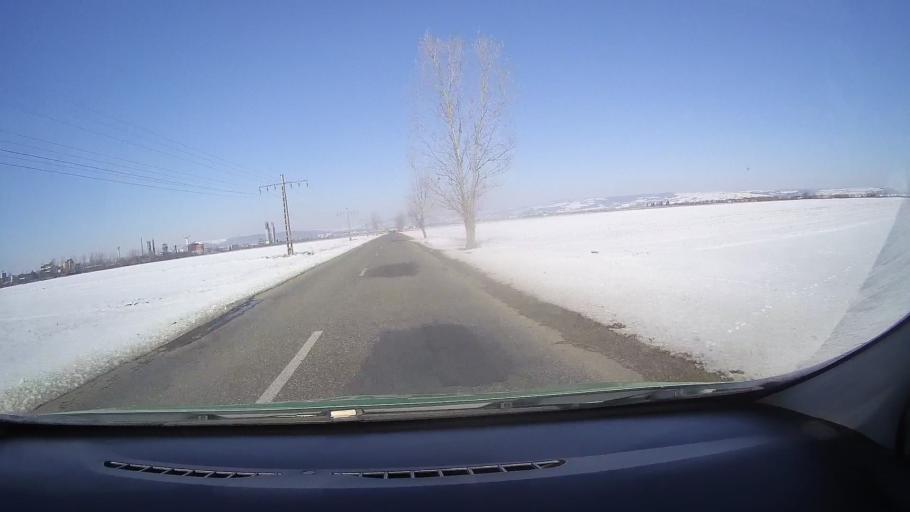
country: RO
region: Brasov
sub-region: Comuna Harseni
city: Harseni
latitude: 45.7997
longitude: 24.9933
